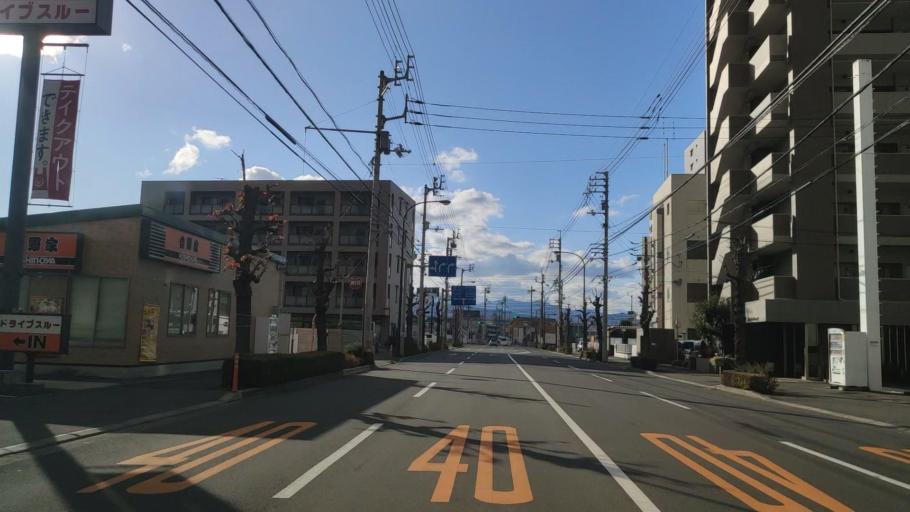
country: JP
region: Ehime
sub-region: Shikoku-chuo Shi
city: Matsuyama
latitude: 33.8316
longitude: 132.7525
